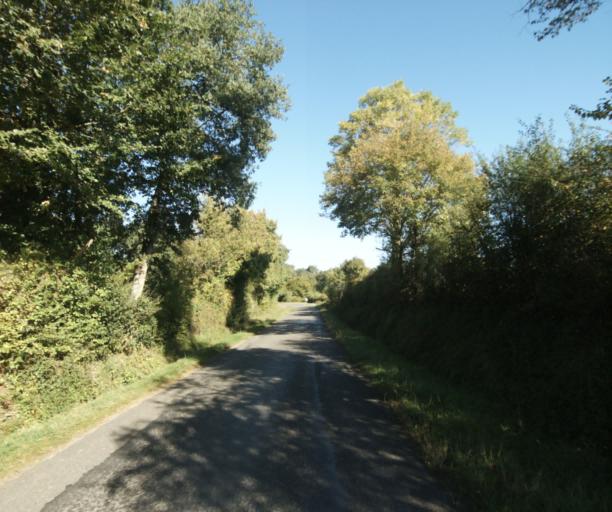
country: FR
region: Midi-Pyrenees
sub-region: Departement du Gers
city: Gondrin
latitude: 43.8125
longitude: 0.2255
